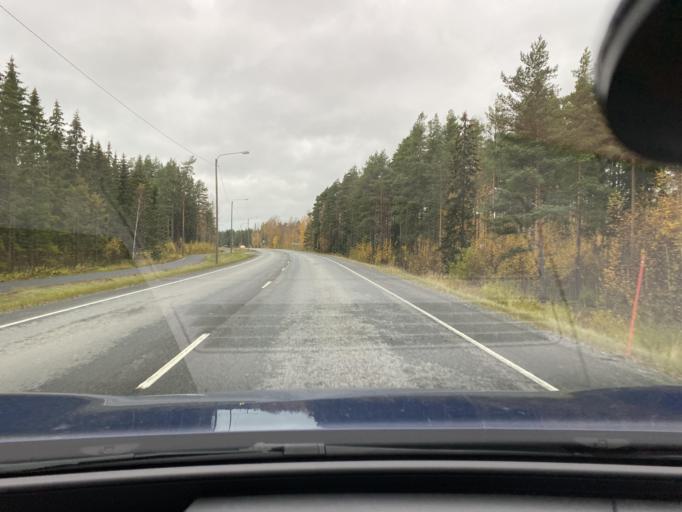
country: FI
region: Satakunta
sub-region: Rauma
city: Rauma
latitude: 61.1358
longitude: 21.5861
